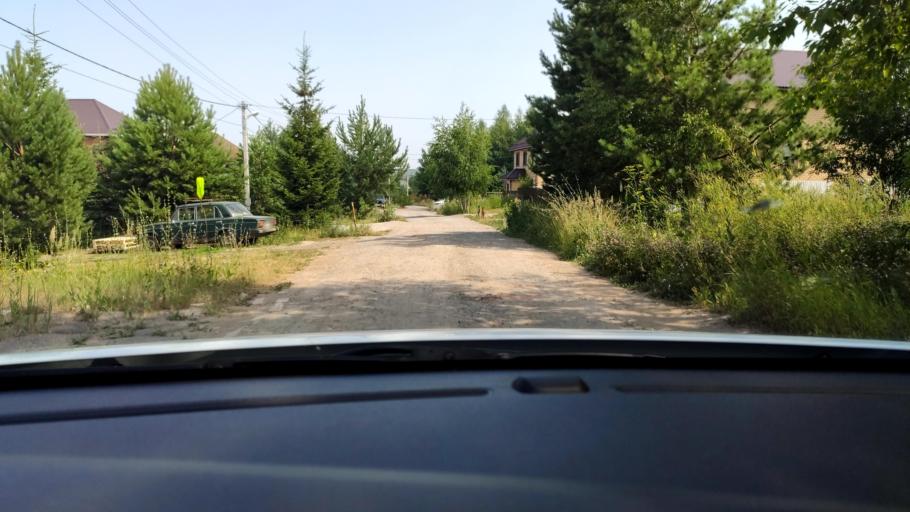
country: RU
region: Tatarstan
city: Stolbishchi
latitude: 55.7433
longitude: 49.2519
